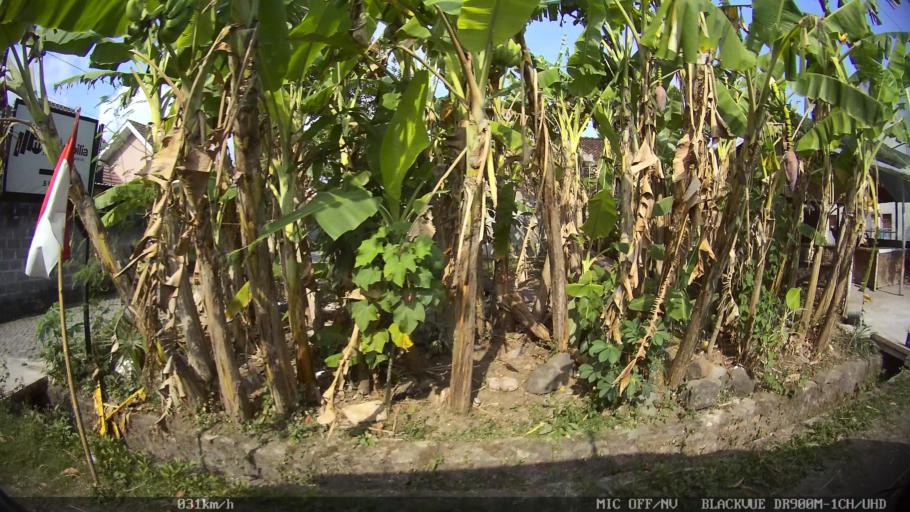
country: ID
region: Daerah Istimewa Yogyakarta
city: Kasihan
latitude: -7.8336
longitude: 110.3234
